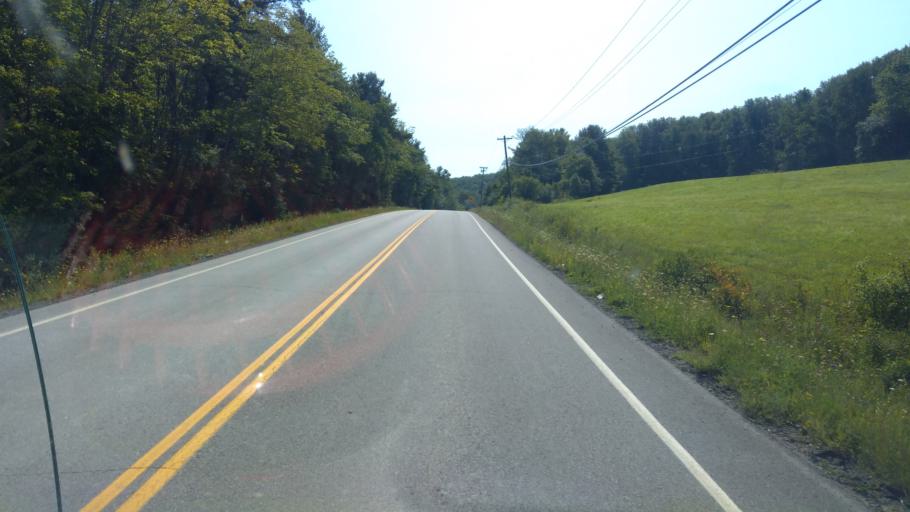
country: US
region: New York
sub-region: Allegany County
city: Belmont
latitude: 42.2948
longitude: -78.0063
